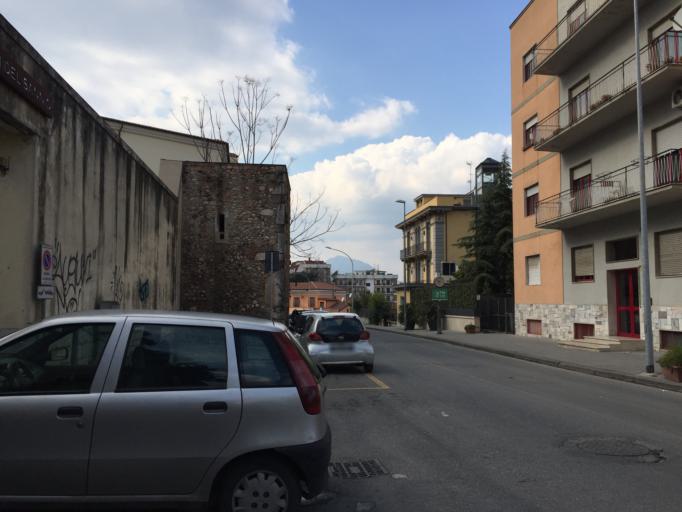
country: IT
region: Campania
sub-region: Provincia di Benevento
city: Benevento
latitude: 41.1324
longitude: 14.7812
